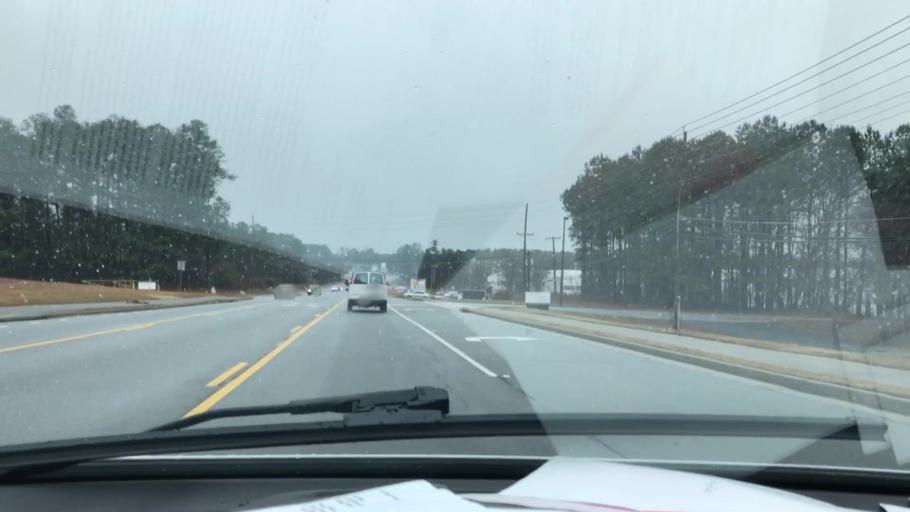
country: US
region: Georgia
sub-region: Gwinnett County
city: Berkeley Lake
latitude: 33.9804
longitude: -84.1676
